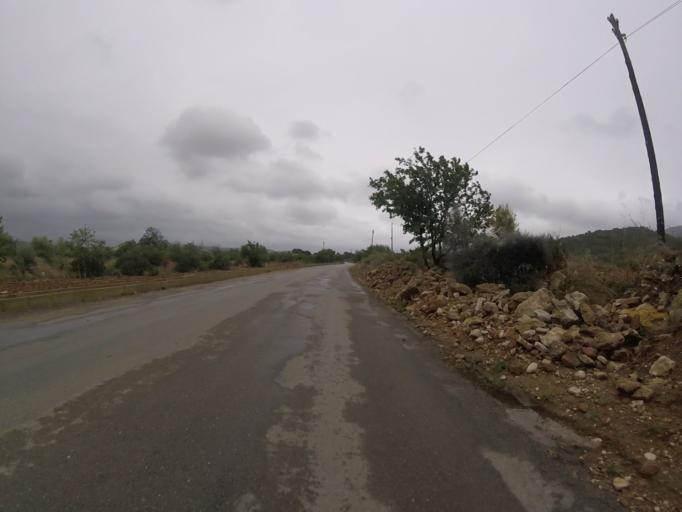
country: ES
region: Valencia
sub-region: Provincia de Castello
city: Alcoceber
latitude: 40.2459
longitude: 0.2471
